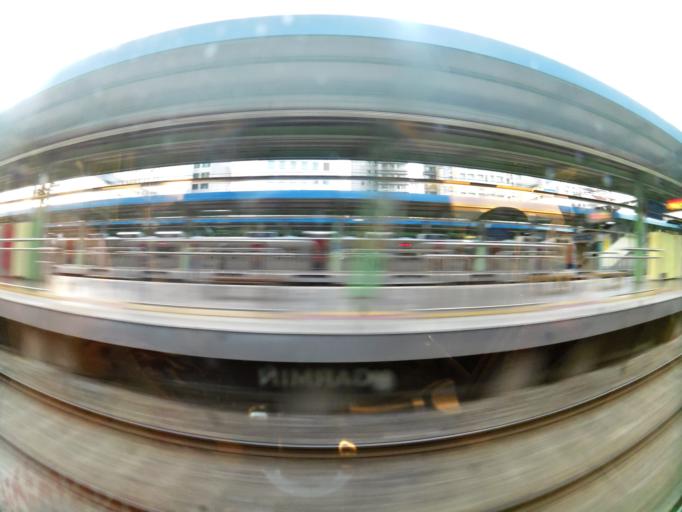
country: KR
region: Gyeonggi-do
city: Kwangmyong
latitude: 37.5030
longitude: 126.8823
